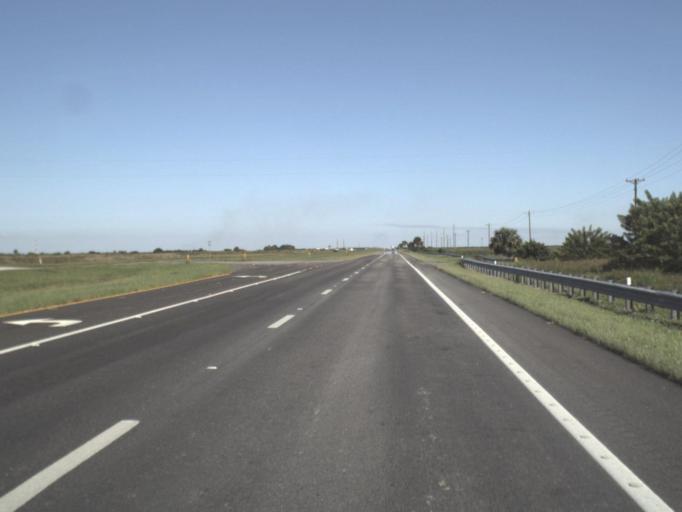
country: US
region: Florida
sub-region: Glades County
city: Moore Haven
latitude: 26.7528
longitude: -81.1217
